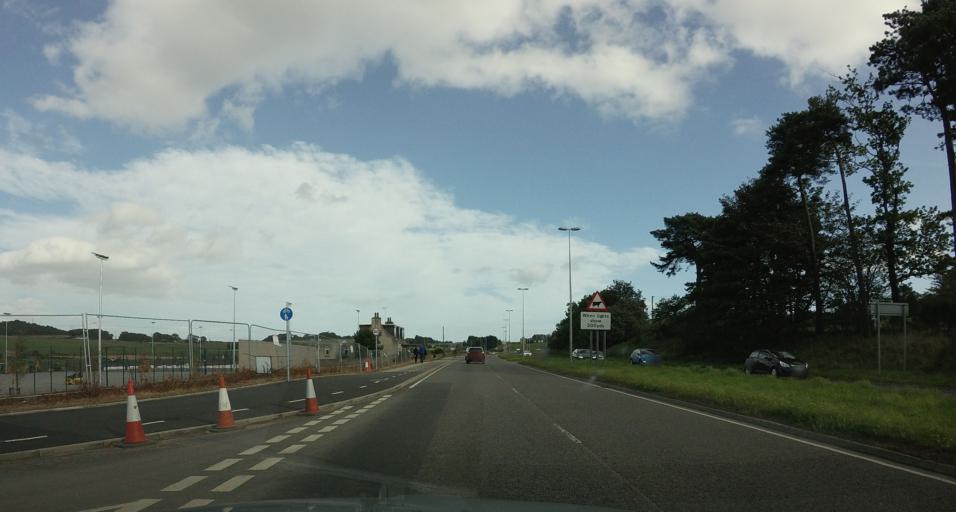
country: GB
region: Scotland
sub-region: Aberdeenshire
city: Westhill
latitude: 57.1473
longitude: -2.2587
